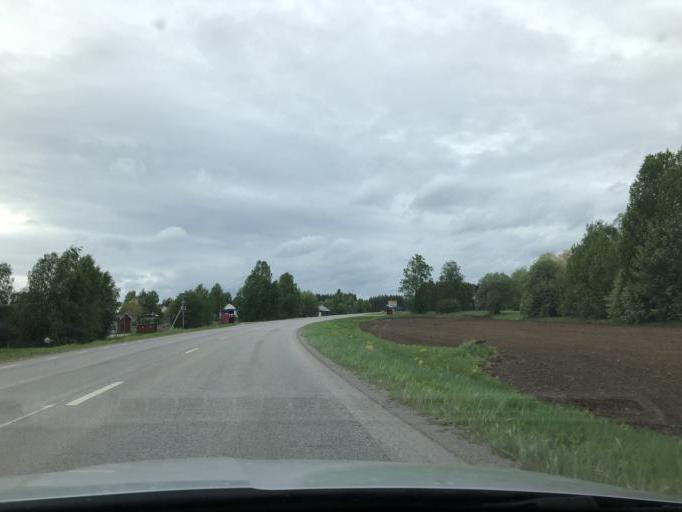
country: SE
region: Norrbotten
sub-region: Pitea Kommun
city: Bergsviken
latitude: 65.3534
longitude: 21.3865
